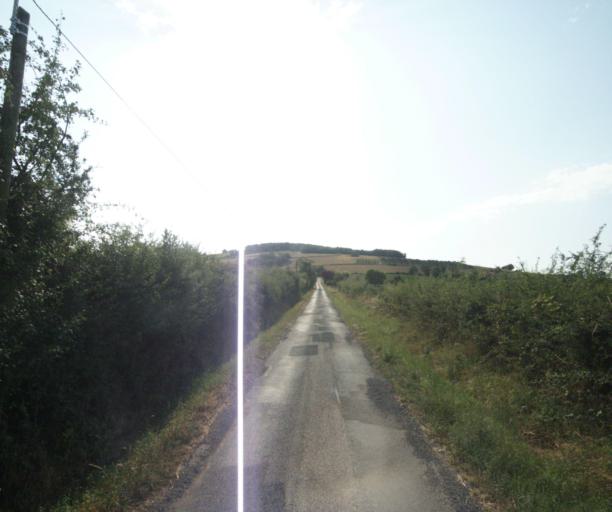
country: FR
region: Rhone-Alpes
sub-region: Departement du Rhone
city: Savigny
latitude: 45.8304
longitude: 4.5758
